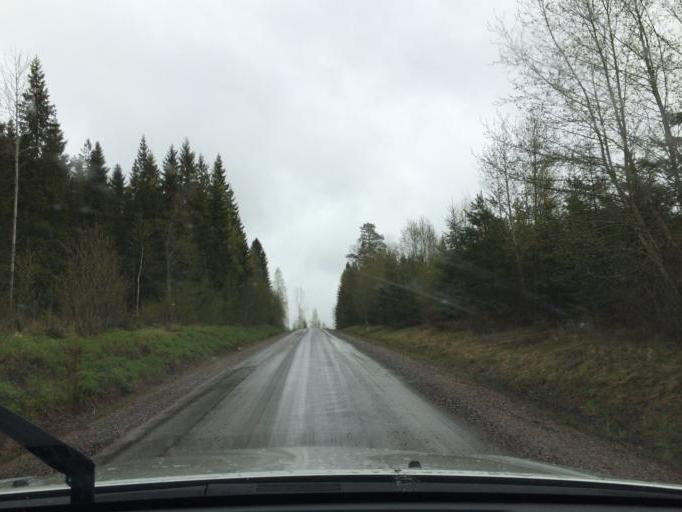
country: SE
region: Dalarna
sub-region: Ludvika Kommun
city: Abborrberget
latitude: 60.0398
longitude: 14.6887
